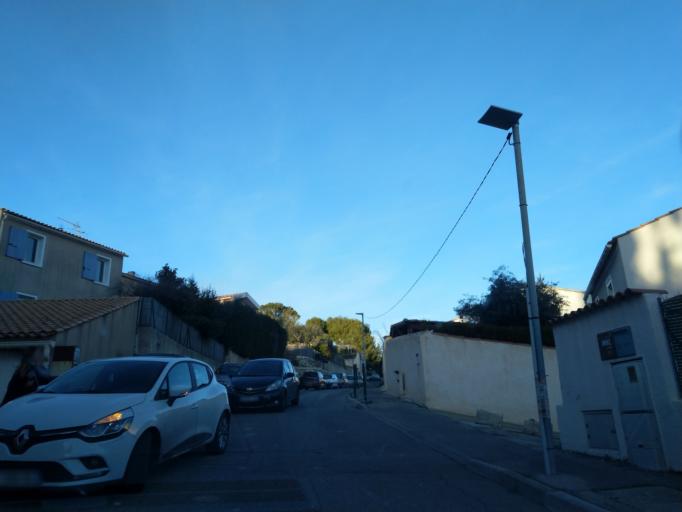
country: FR
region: Provence-Alpes-Cote d'Azur
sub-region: Departement des Bouches-du-Rhone
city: Plan-de-Cuques
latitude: 43.3566
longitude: 5.4628
